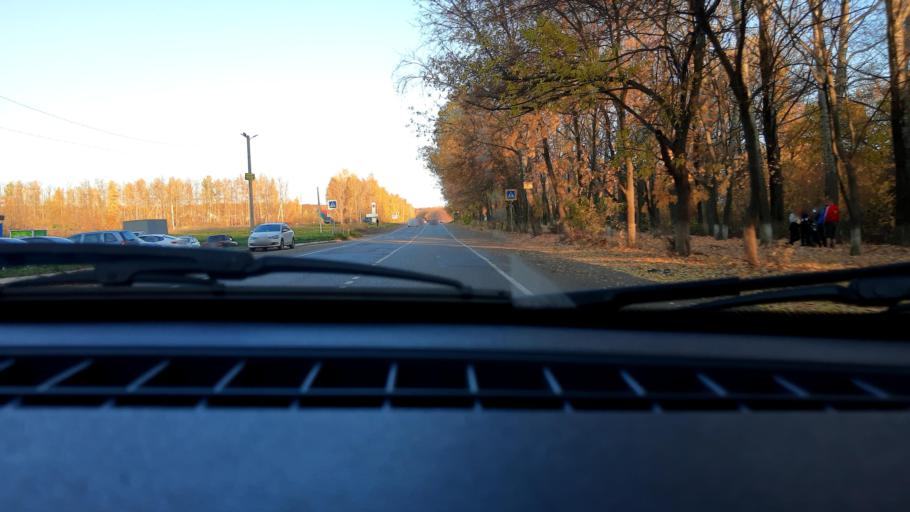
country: RU
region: Bashkortostan
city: Avdon
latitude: 54.8207
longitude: 55.6971
